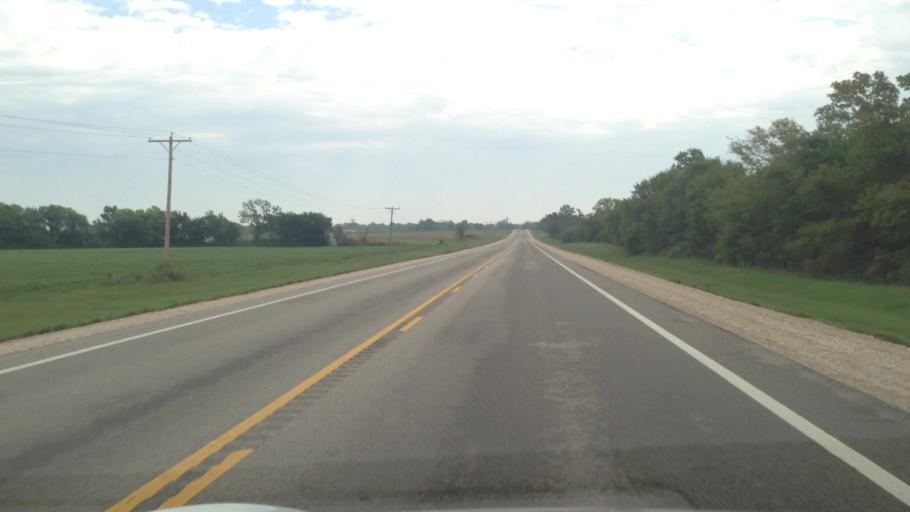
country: US
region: Kansas
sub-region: Allen County
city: Iola
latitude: 37.9043
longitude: -95.0923
